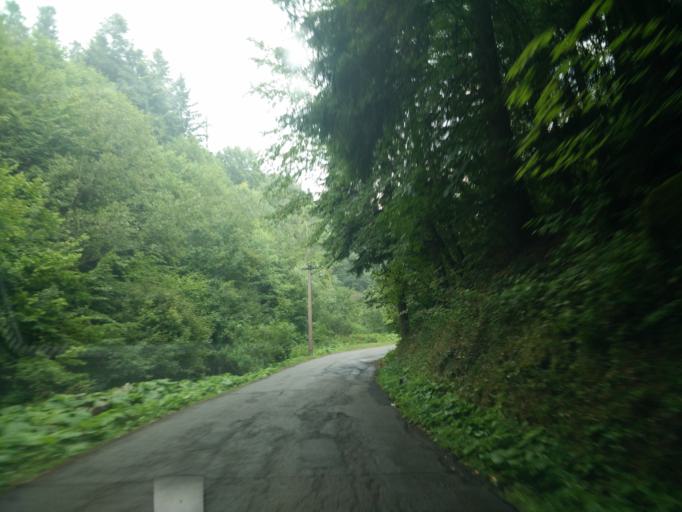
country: SK
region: Banskobystricky
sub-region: Okres Banska Bystrica
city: Banska Stiavnica
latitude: 48.4886
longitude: 18.8511
